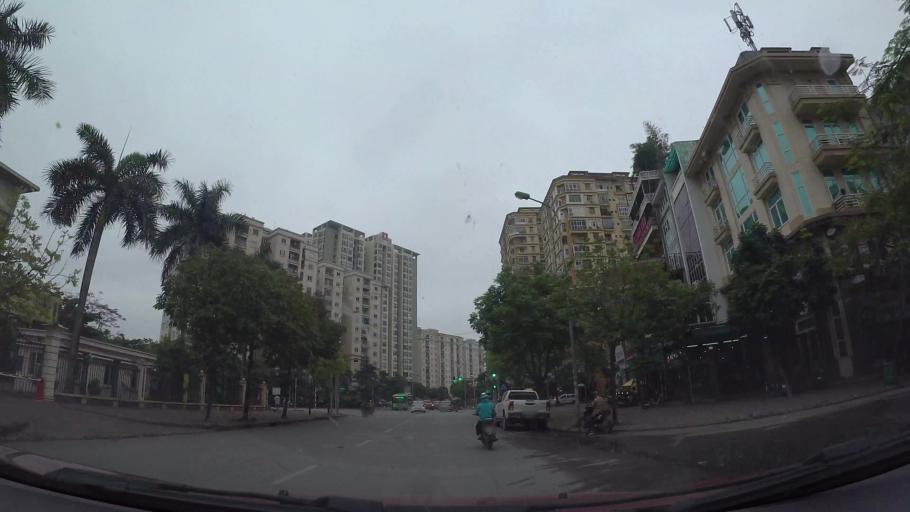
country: VN
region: Ha Noi
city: Cau Giay
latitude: 21.0168
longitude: 105.7983
